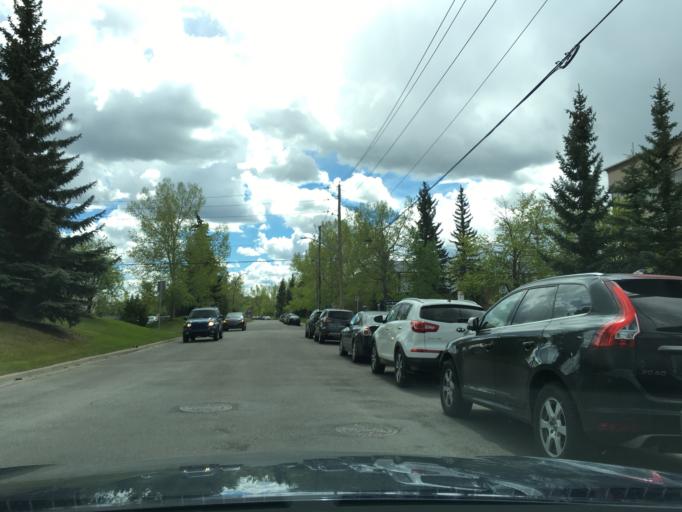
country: CA
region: Alberta
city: Calgary
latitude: 50.9098
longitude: -114.0633
